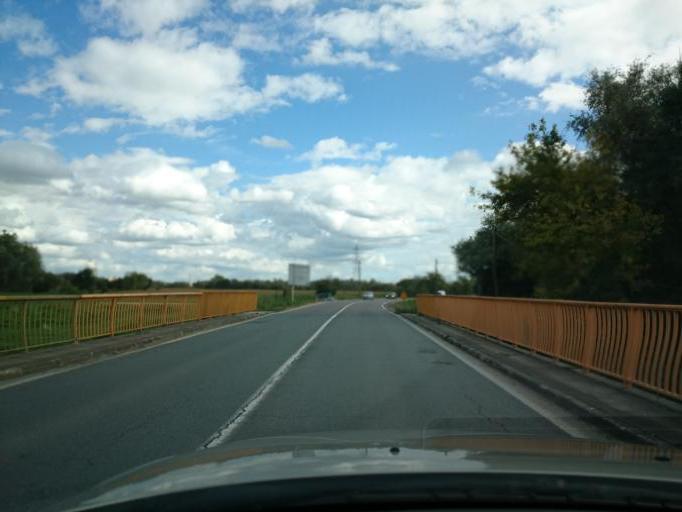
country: FR
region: Aquitaine
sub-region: Departement de la Gironde
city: Saint-Louis-de-Montferrand
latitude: 44.9136
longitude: -0.5613
